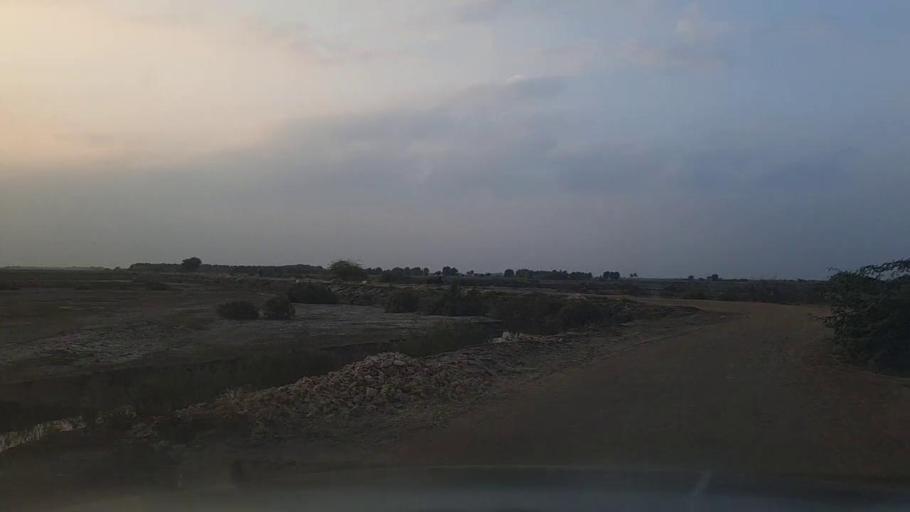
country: PK
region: Sindh
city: Jati
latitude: 24.5294
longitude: 68.4081
